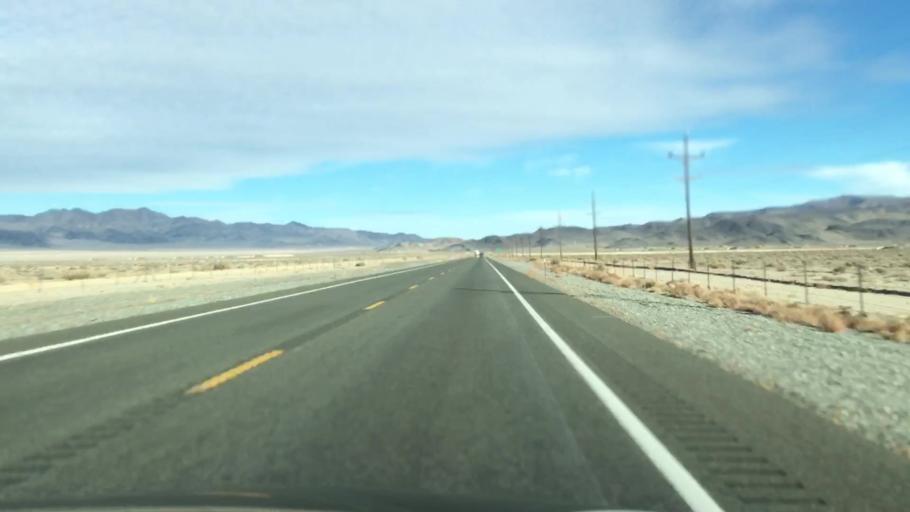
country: US
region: Nevada
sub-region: Mineral County
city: Hawthorne
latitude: 38.5257
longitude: -118.5712
